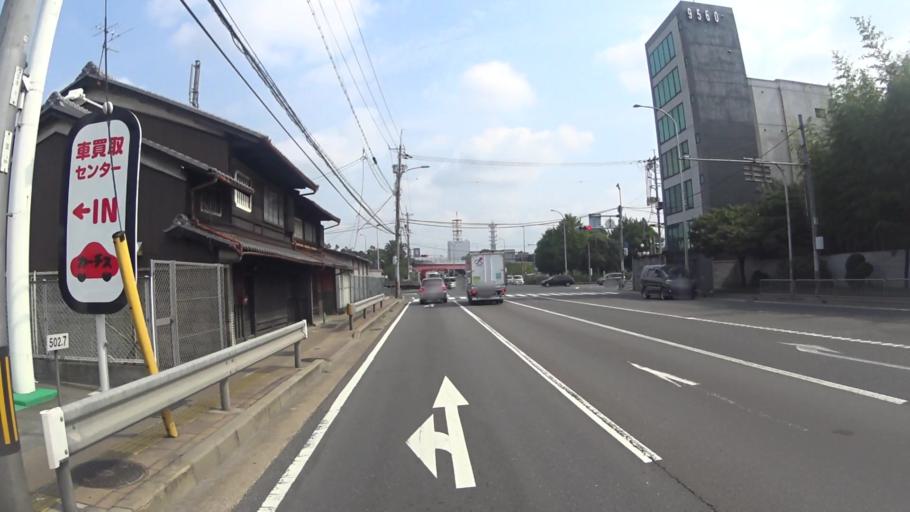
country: JP
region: Kyoto
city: Muko
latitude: 34.9508
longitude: 135.7454
